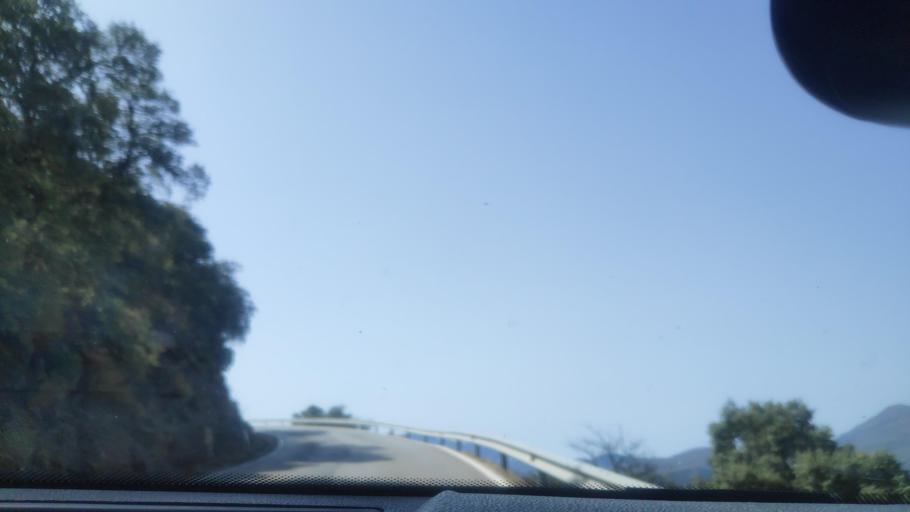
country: ES
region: Andalusia
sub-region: Provincia de Granada
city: Pampaneira
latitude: 36.9252
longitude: -3.3537
